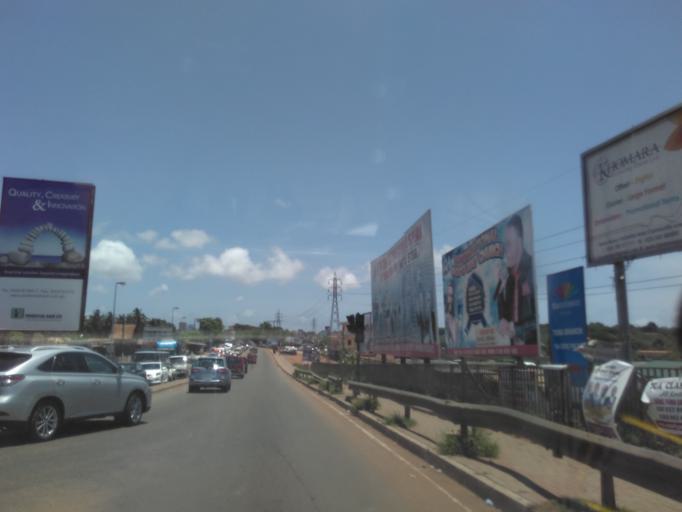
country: GH
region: Greater Accra
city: Tema
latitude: 5.6812
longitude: -0.0250
